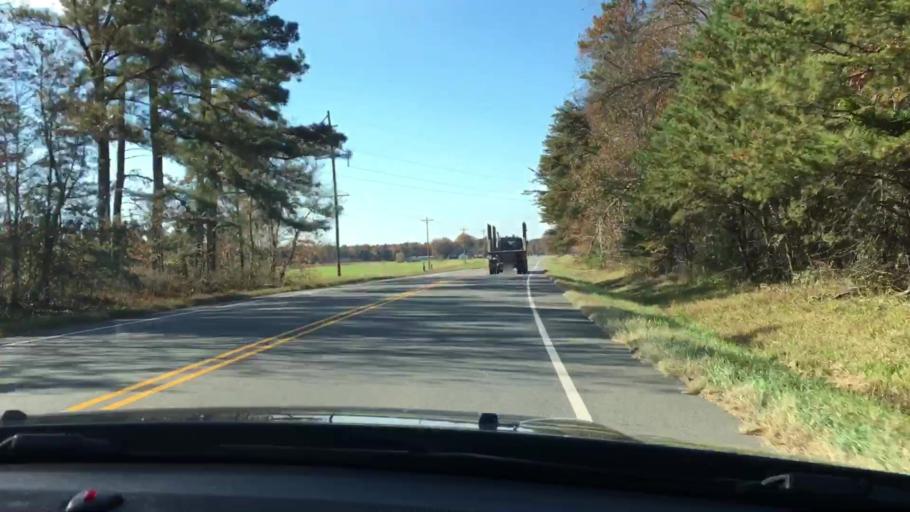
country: US
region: Virginia
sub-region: Hanover County
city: Hanover
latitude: 37.8117
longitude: -77.2915
